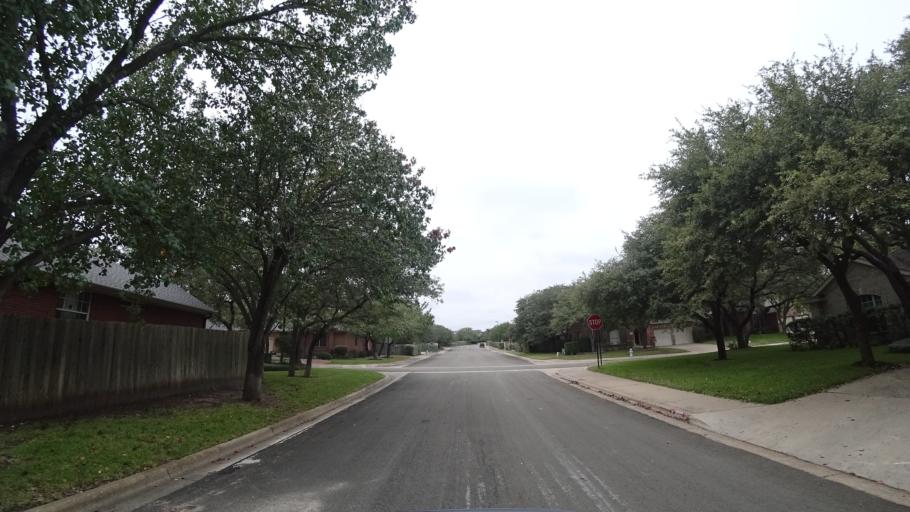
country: US
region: Texas
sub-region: Travis County
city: Shady Hollow
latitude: 30.2121
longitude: -97.8849
